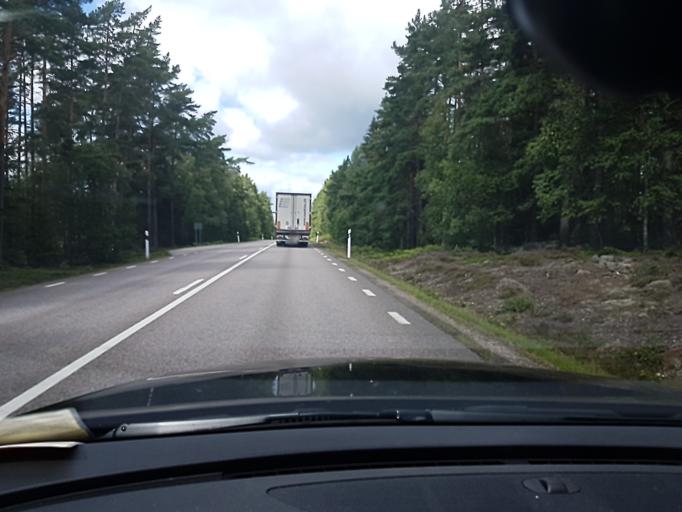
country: SE
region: Kronoberg
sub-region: Lessebo Kommun
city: Hovmantorp
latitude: 56.7878
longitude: 15.1470
